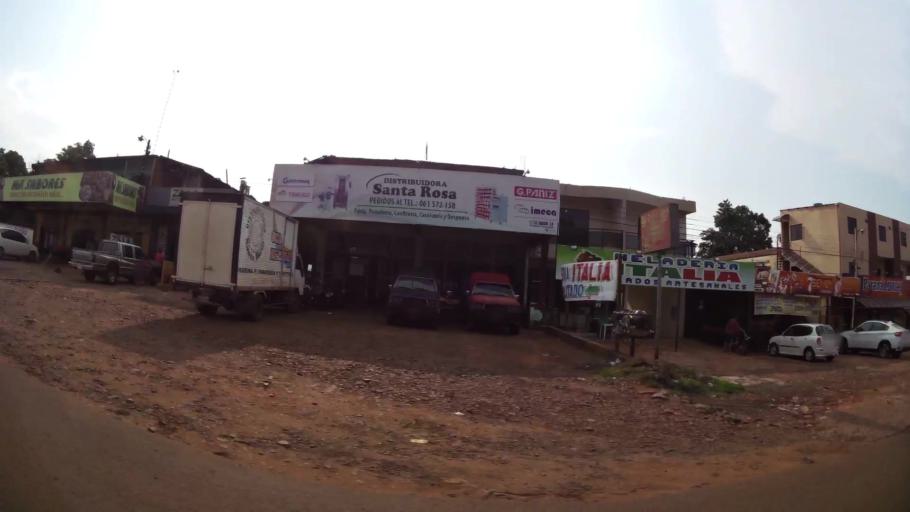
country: PY
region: Alto Parana
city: Ciudad del Este
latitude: -25.4971
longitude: -54.6630
